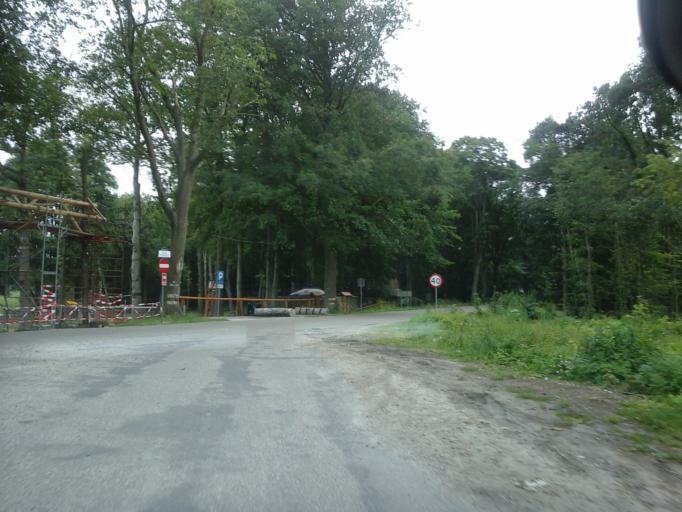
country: PL
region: West Pomeranian Voivodeship
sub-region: Powiat choszczenski
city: Bierzwnik
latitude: 53.0122
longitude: 15.6385
